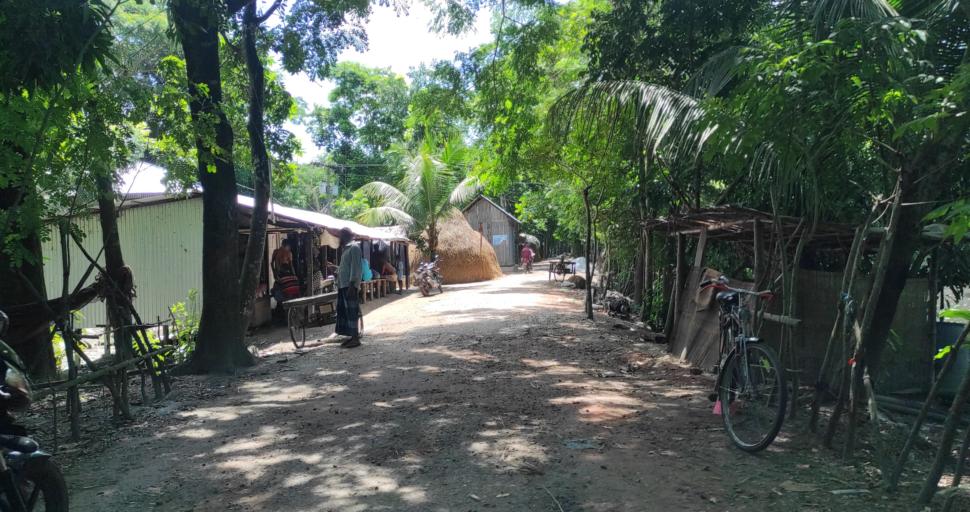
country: BD
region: Barisal
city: Gaurnadi
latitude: 22.9183
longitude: 90.0807
